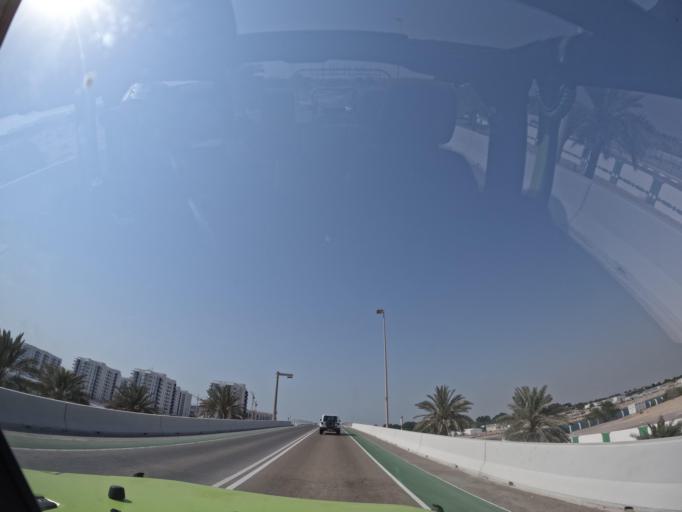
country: AE
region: Abu Dhabi
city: Abu Dhabi
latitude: 24.4804
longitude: 54.6245
